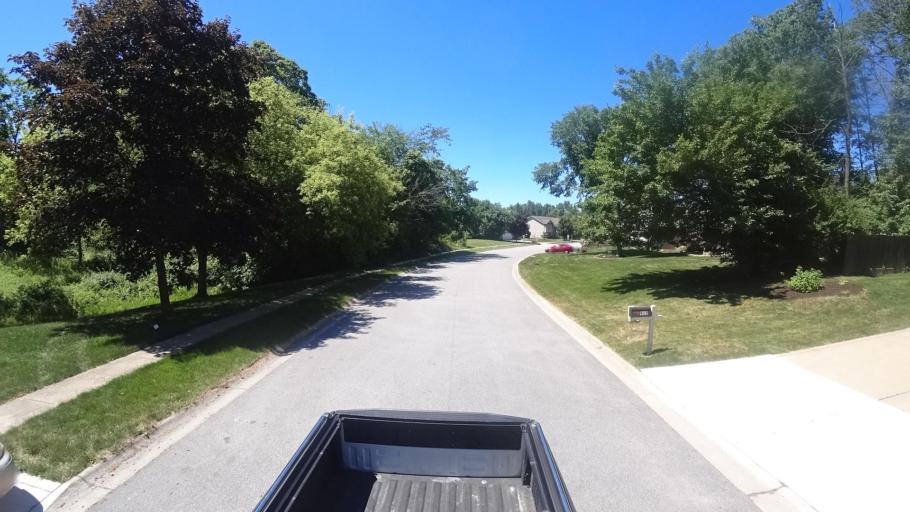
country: US
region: Indiana
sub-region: Porter County
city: Porter
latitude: 41.6283
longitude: -87.0710
